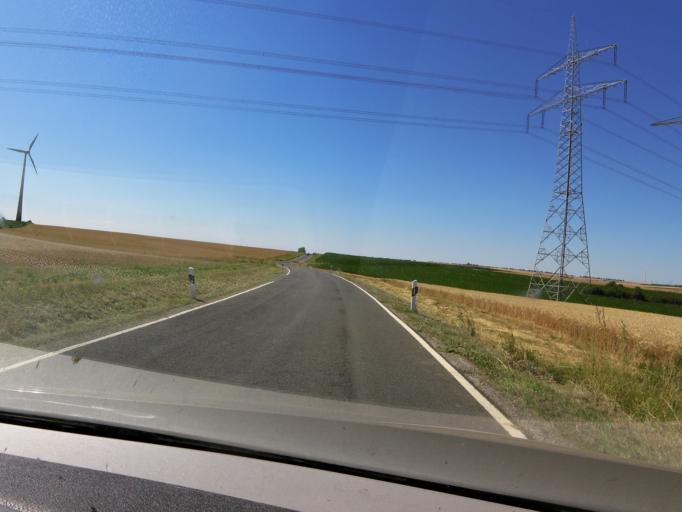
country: DE
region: Bavaria
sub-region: Regierungsbezirk Unterfranken
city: Theilheim
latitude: 49.7491
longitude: 10.0557
